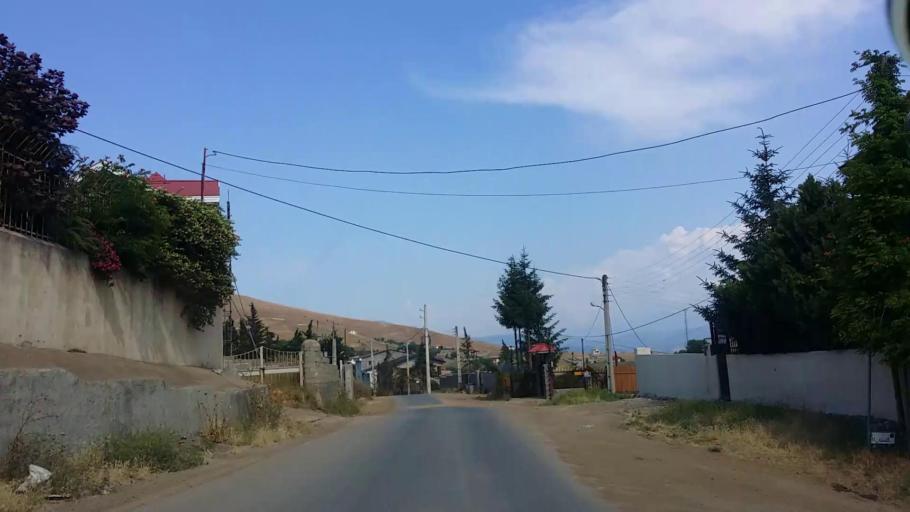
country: IR
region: Mazandaran
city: Chalus
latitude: 36.5157
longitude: 51.2483
